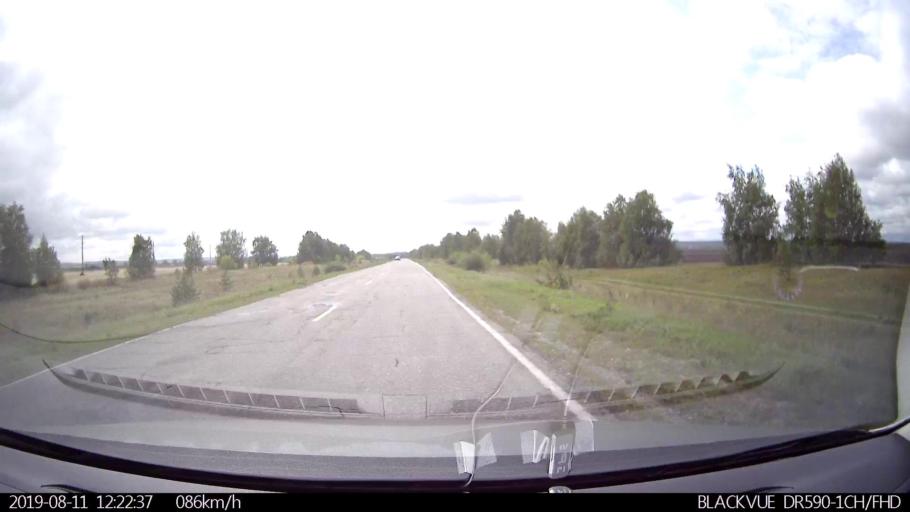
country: RU
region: Ulyanovsk
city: Ignatovka
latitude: 53.9055
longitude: 47.9516
